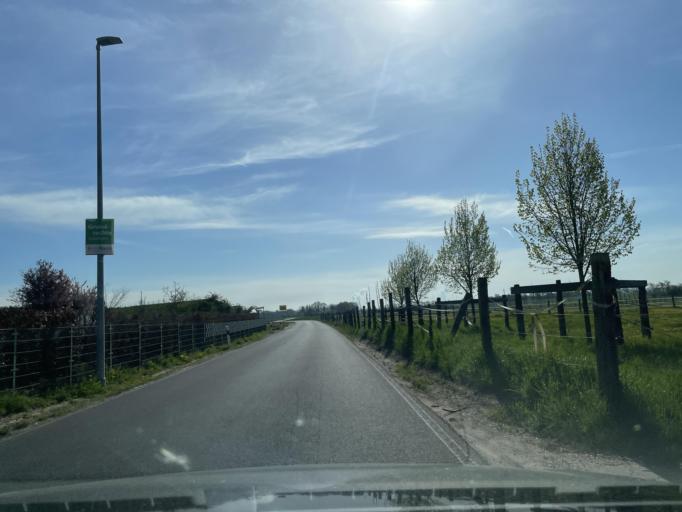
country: DE
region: North Rhine-Westphalia
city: Erkelenz
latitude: 51.0818
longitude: 6.3704
